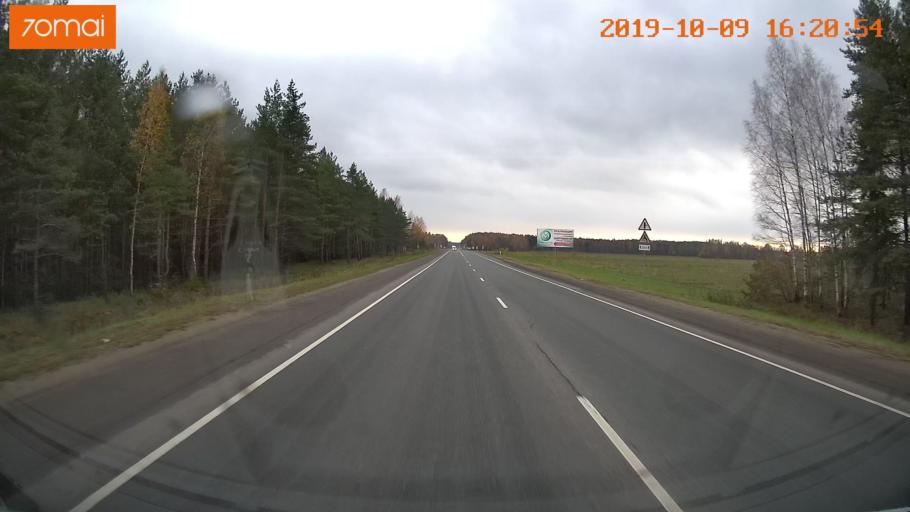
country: RU
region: Kostroma
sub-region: Kostromskoy Rayon
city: Kostroma
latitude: 57.7004
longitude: 40.8909
